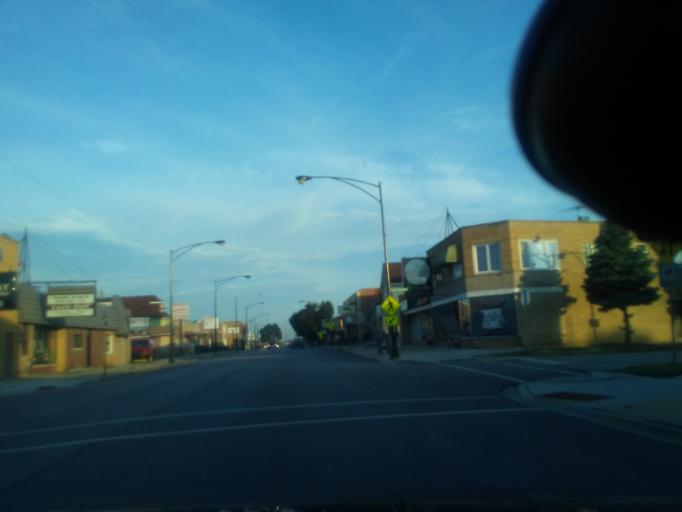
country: US
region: Illinois
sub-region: Cook County
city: Harwood Heights
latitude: 41.9803
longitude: -87.8034
